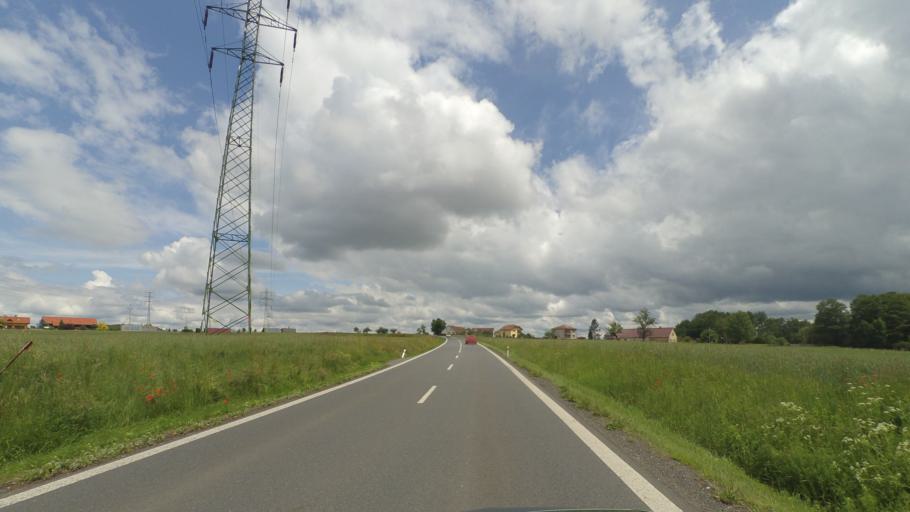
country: CZ
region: Plzensky
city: Klatovy
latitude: 49.3743
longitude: 13.2645
